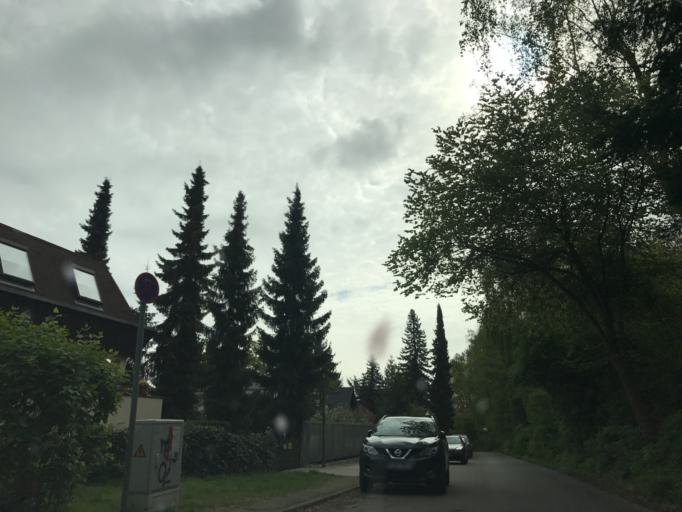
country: DE
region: Berlin
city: Wilhelmstadt
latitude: 52.5076
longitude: 13.1842
